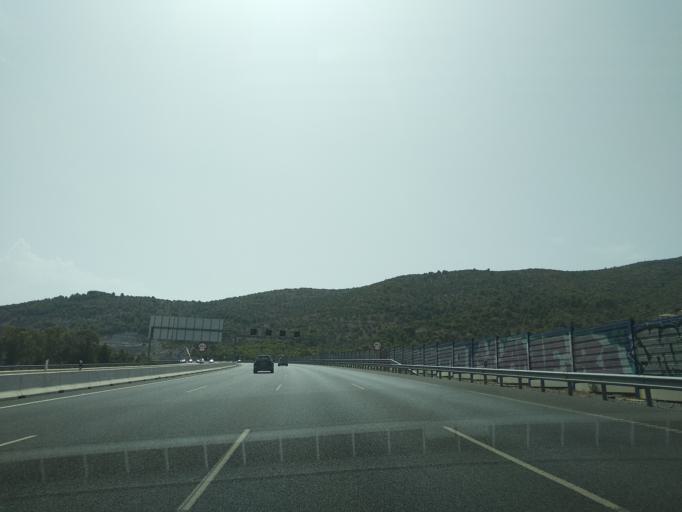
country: ES
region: Andalusia
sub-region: Provincia de Malaga
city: Alhaurin de la Torre
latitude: 36.6631
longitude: -4.5279
